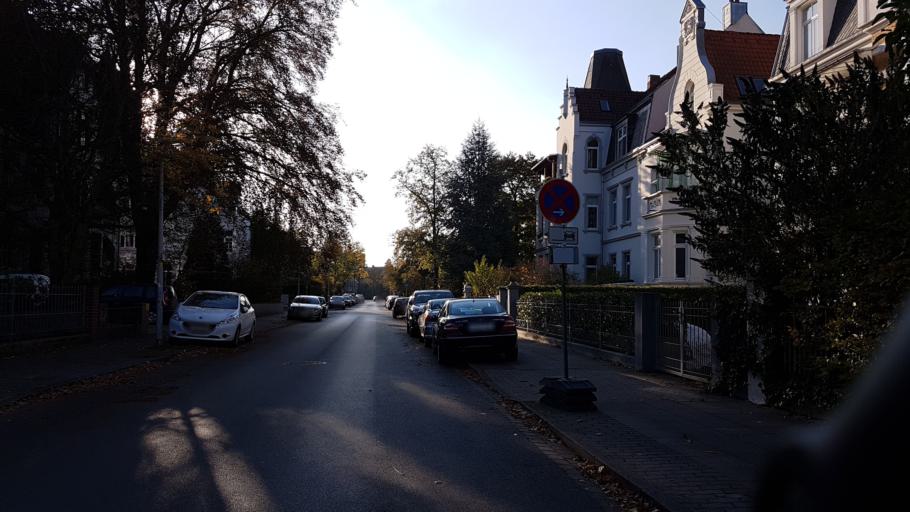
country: DE
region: Lower Saxony
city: Hannover
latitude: 52.3467
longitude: 9.7646
